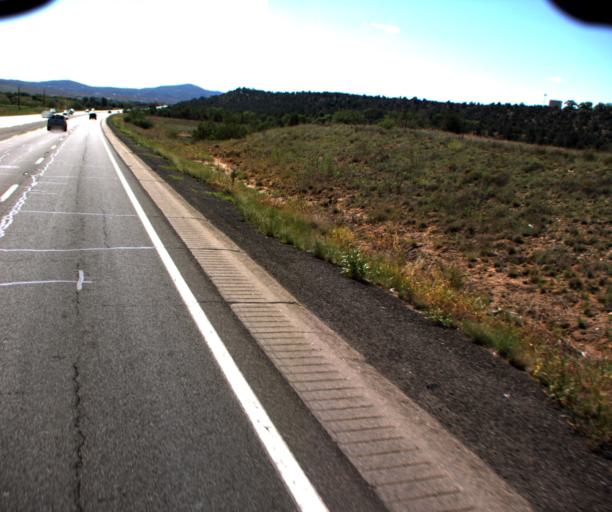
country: US
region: Arizona
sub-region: Yavapai County
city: Prescott Valley
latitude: 34.5733
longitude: -112.2796
